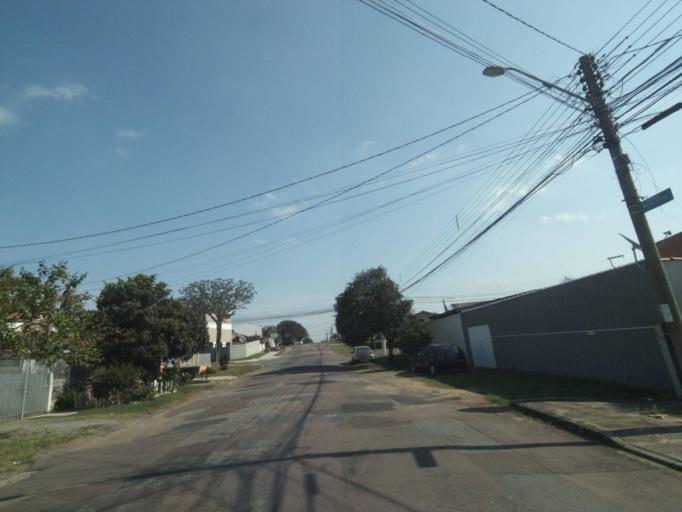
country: BR
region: Parana
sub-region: Curitiba
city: Curitiba
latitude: -25.4859
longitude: -49.3232
